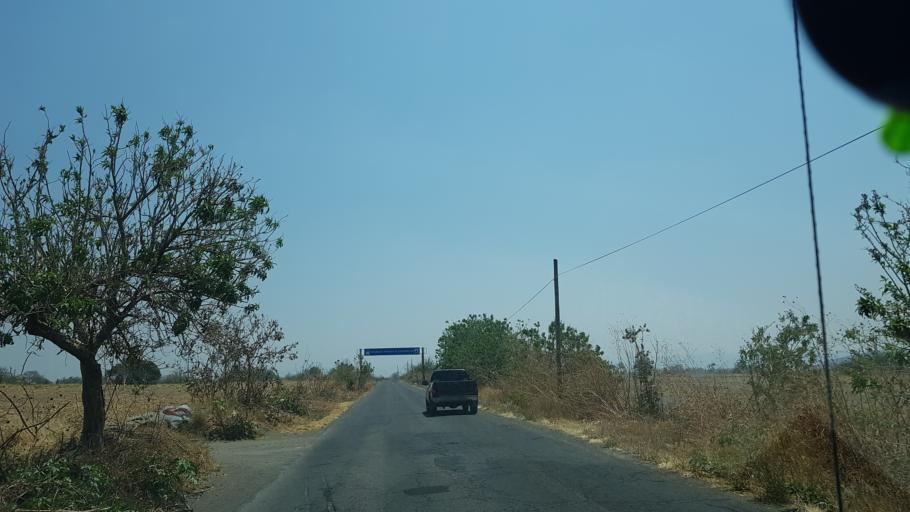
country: MX
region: Puebla
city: Tochimilco
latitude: 18.8871
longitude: -98.5435
